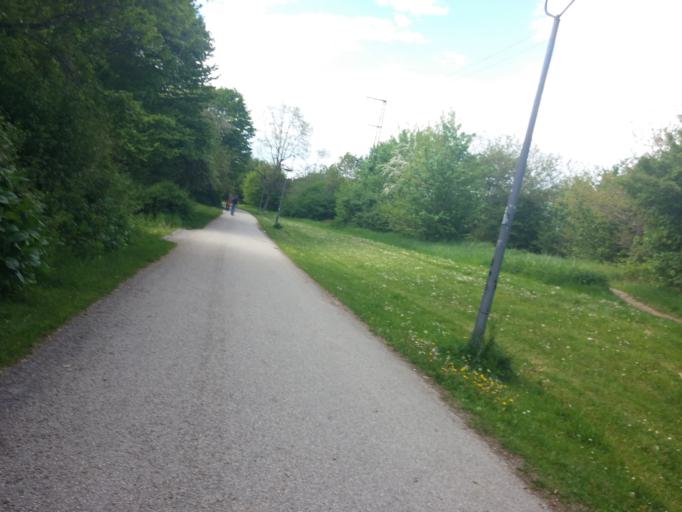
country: DE
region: Bavaria
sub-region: Upper Bavaria
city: Bogenhausen
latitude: 48.1446
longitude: 11.6495
